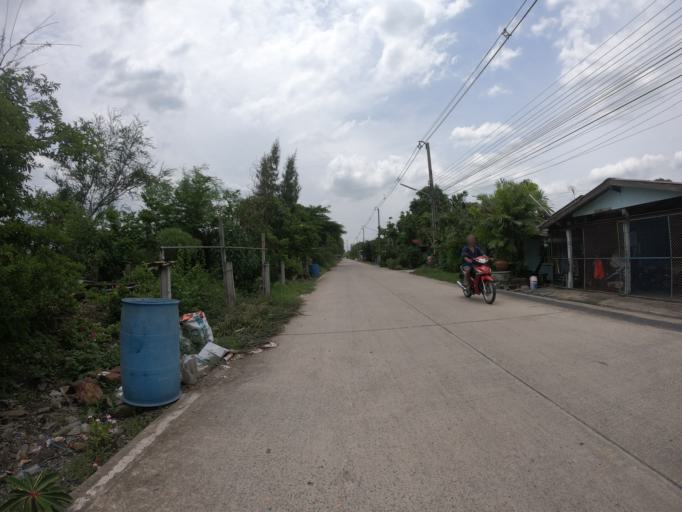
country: TH
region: Pathum Thani
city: Ban Lam Luk Ka
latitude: 14.0003
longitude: 100.8658
